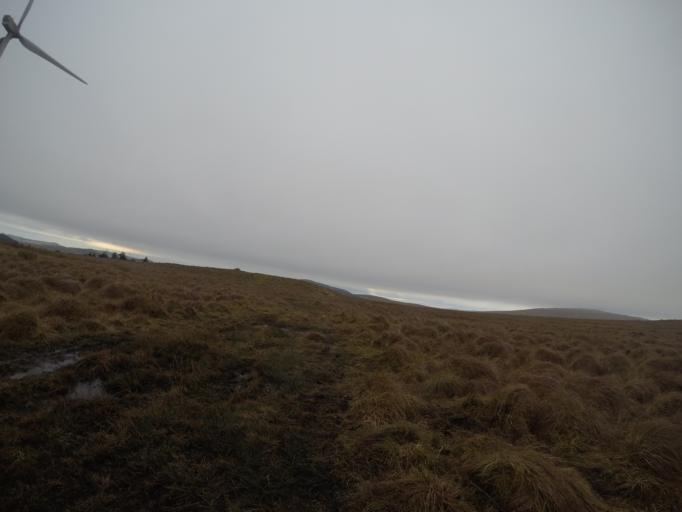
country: GB
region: Scotland
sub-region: North Ayrshire
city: Fairlie
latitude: 55.7377
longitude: -4.7895
